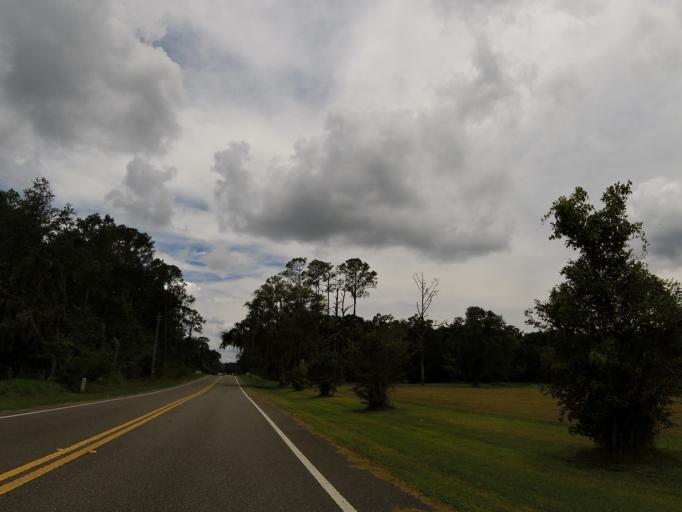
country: US
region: Florida
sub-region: Putnam County
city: East Palatka
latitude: 29.7216
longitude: -81.4955
